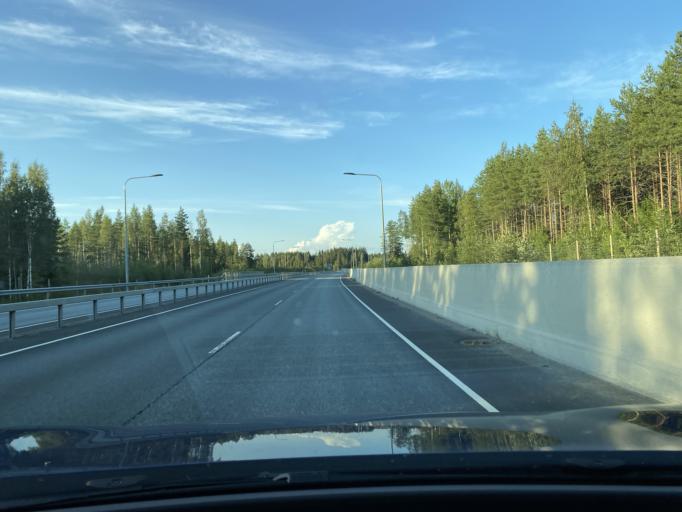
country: FI
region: Southern Ostrobothnia
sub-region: Seinaejoki
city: Seinaejoki
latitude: 62.7020
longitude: 22.8203
